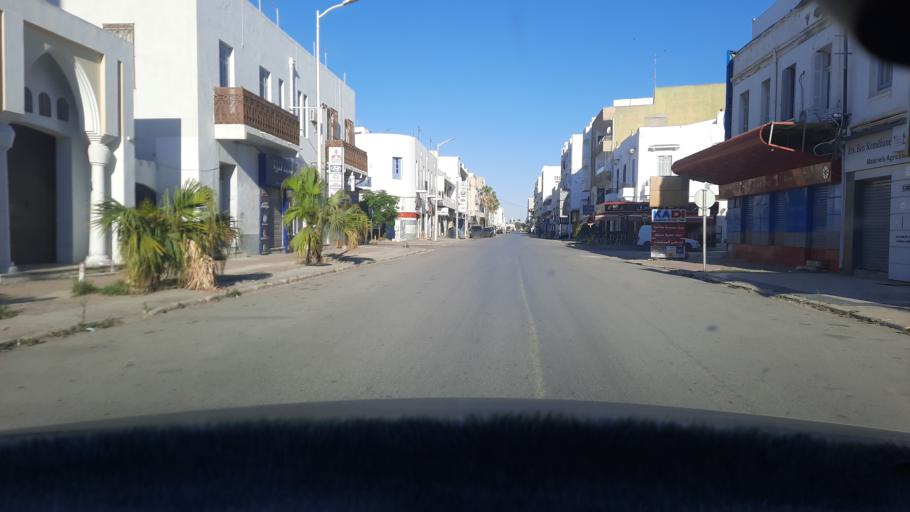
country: TN
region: Safaqis
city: Sfax
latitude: 34.7323
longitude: 10.7554
